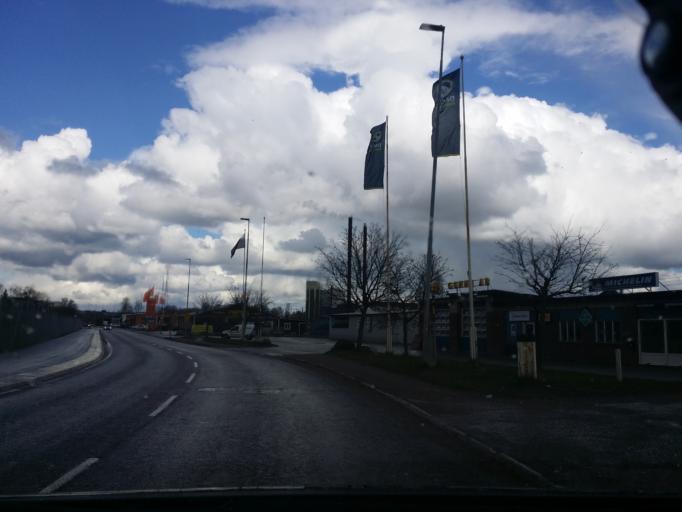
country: SE
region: Vaestmanland
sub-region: Sala Kommun
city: Sala
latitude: 59.9169
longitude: 16.6166
